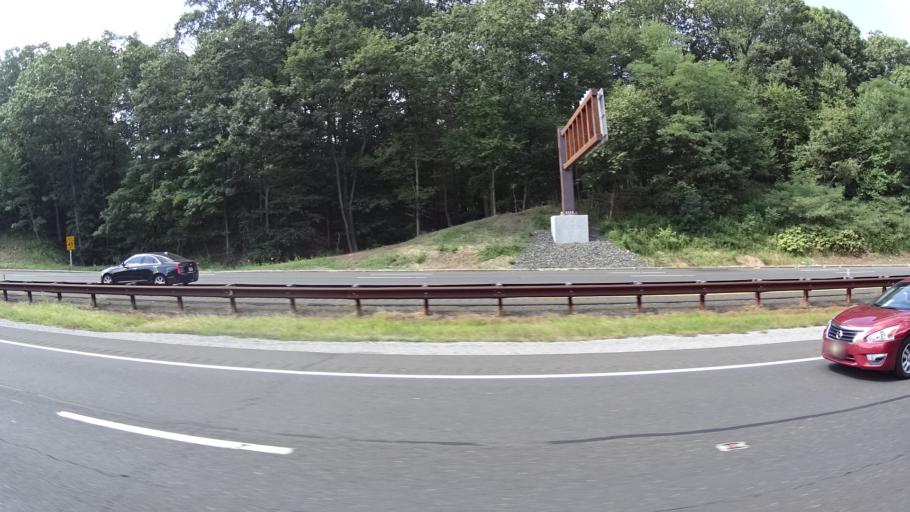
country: US
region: New Jersey
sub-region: Middlesex County
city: Laurence Harbor
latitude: 40.4360
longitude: -74.2539
